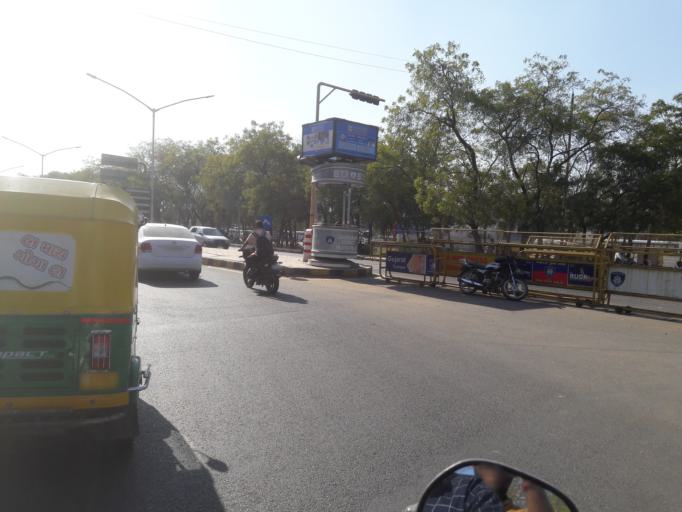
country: IN
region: Gujarat
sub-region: Gandhinagar
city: Ghandinagar
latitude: 23.2161
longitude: 72.6409
